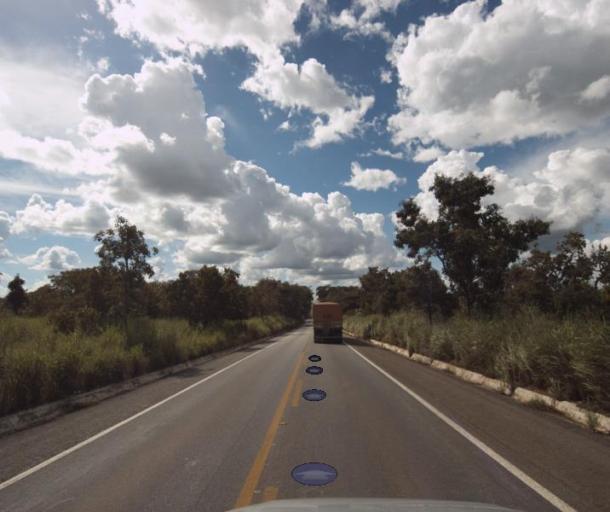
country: BR
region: Goias
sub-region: Porangatu
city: Porangatu
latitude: -13.2498
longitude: -49.1388
